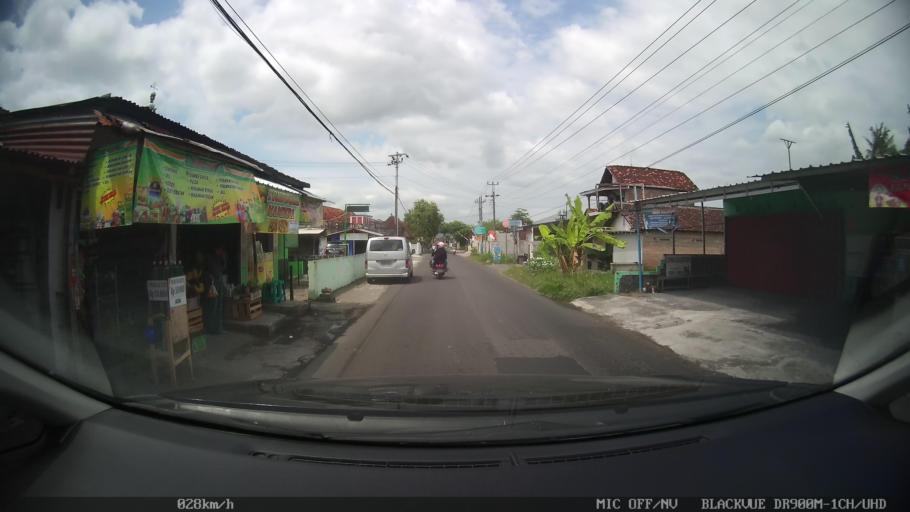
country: ID
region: Daerah Istimewa Yogyakarta
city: Depok
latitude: -7.7777
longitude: 110.4642
